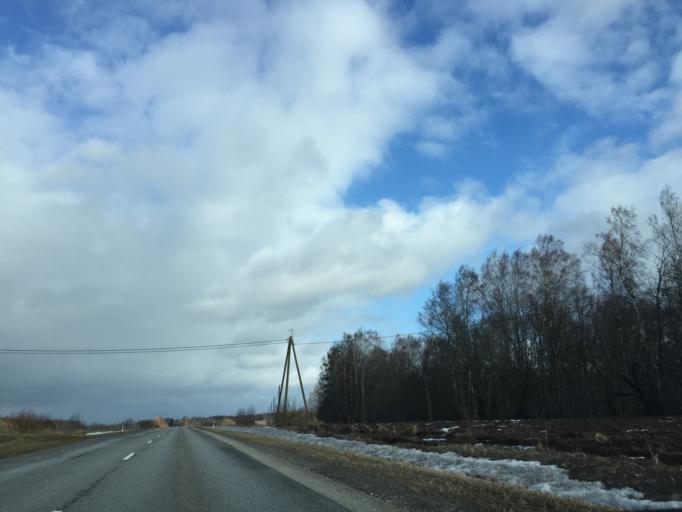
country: LV
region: Aloja
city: Staicele
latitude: 57.8773
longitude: 24.5864
